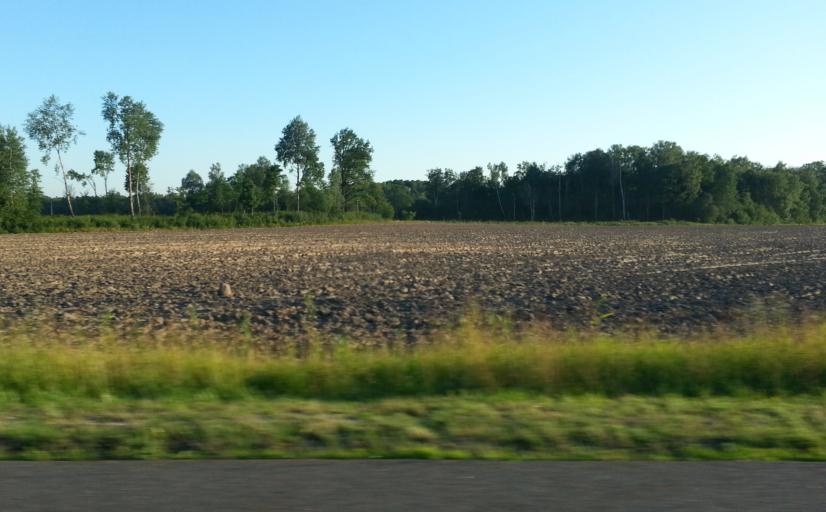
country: LT
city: Ramygala
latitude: 55.5560
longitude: 24.5102
